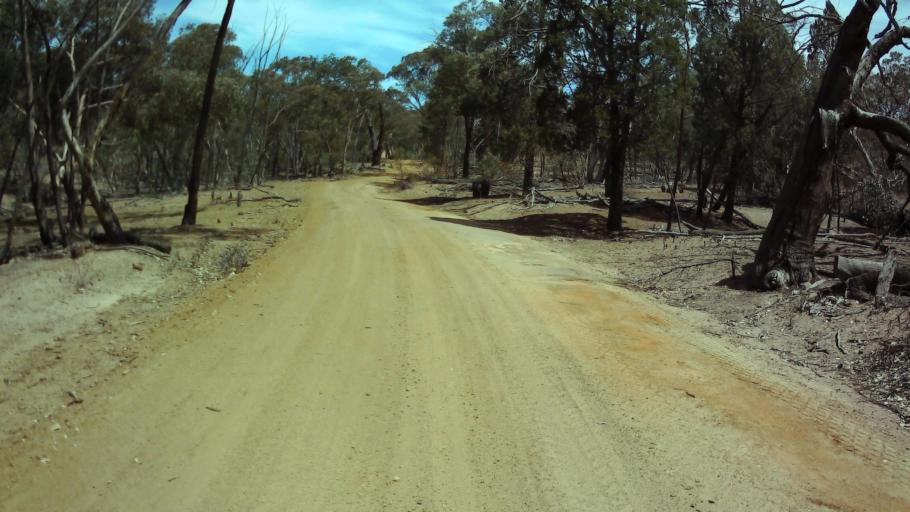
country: AU
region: New South Wales
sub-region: Weddin
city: Grenfell
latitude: -33.7999
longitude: 148.1596
